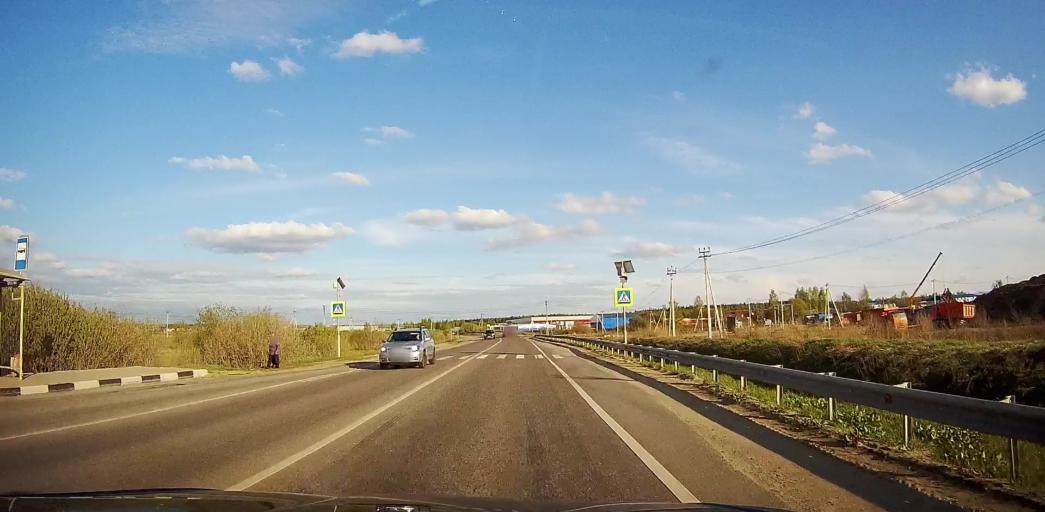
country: RU
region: Moskovskaya
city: Malyshevo
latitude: 55.4878
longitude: 38.3225
